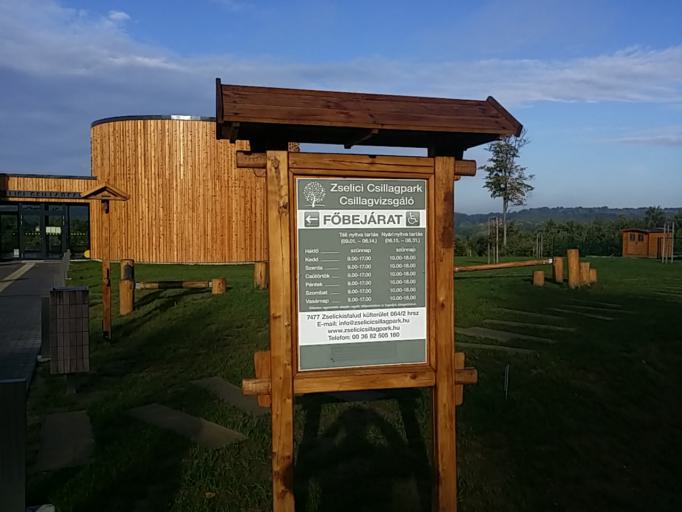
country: HU
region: Somogy
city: Kaposvar
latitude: 46.2365
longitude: 17.7658
